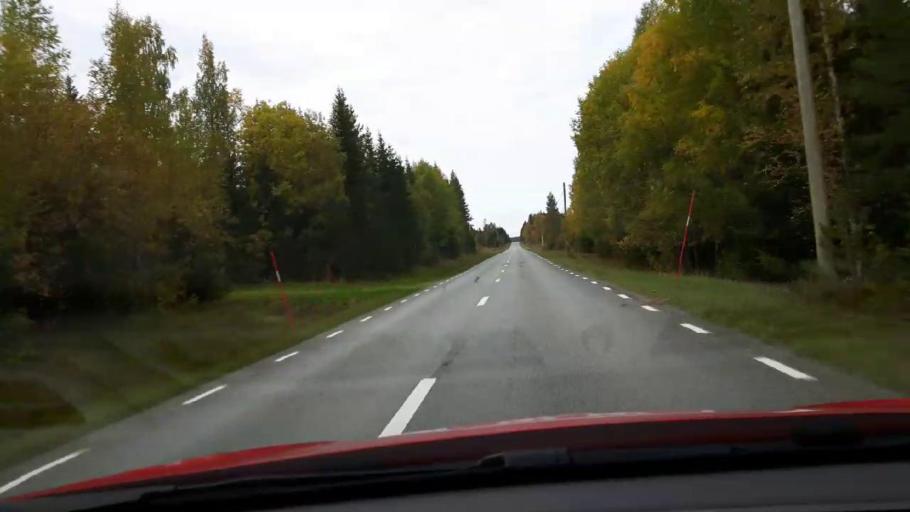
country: SE
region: Jaemtland
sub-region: Krokoms Kommun
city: Krokom
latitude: 63.1924
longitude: 14.0557
